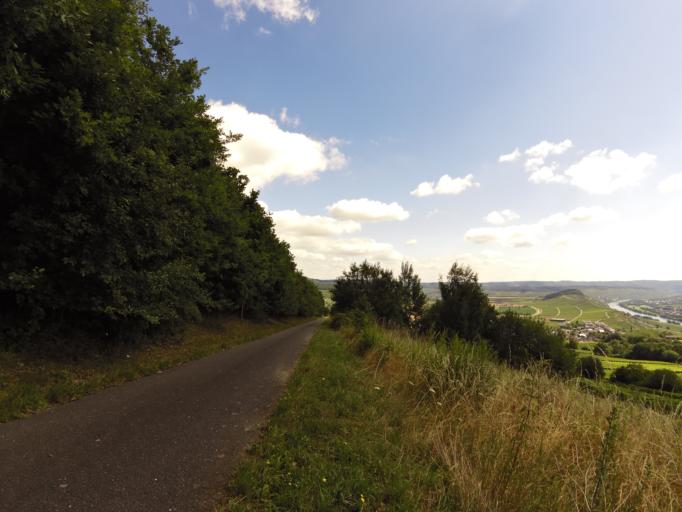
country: DE
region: Rheinland-Pfalz
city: Kesten
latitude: 49.9064
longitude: 6.9434
